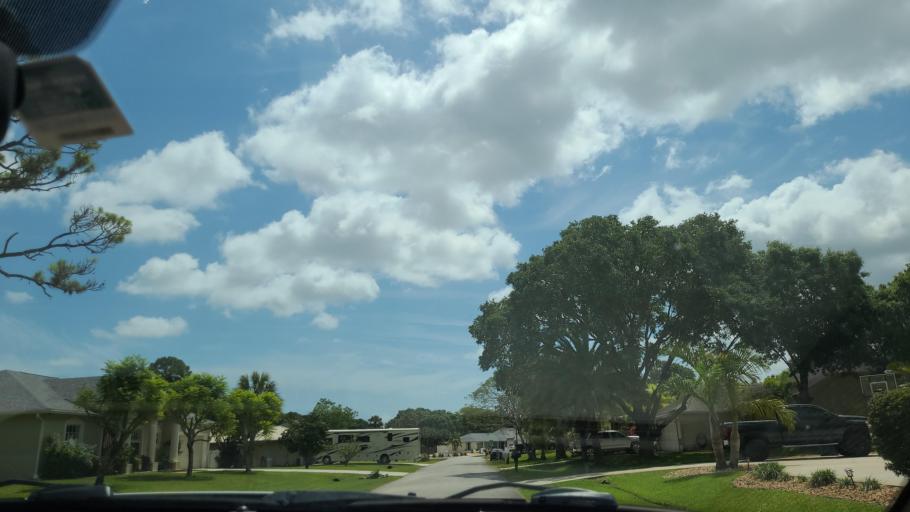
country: US
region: Florida
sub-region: Brevard County
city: West Melbourne
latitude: 28.0214
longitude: -80.6587
